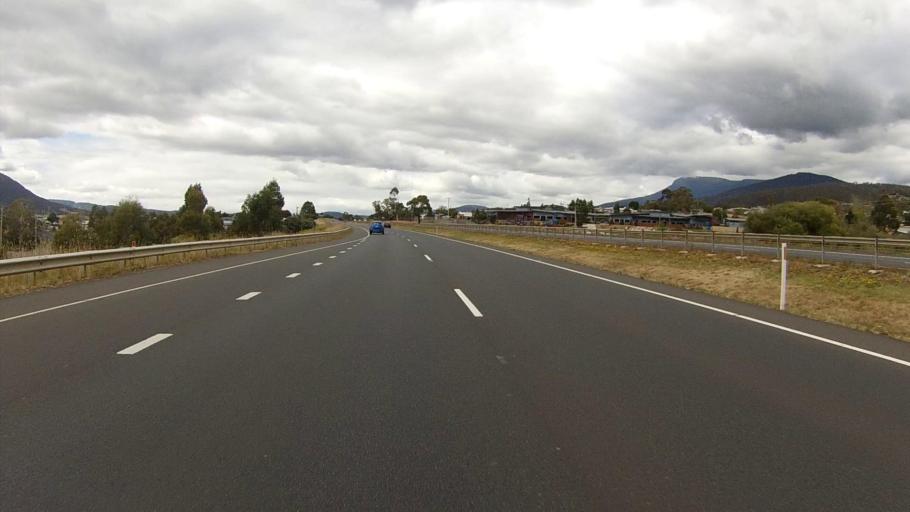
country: AU
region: Tasmania
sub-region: Glenorchy
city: Claremont
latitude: -42.7823
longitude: 147.2395
